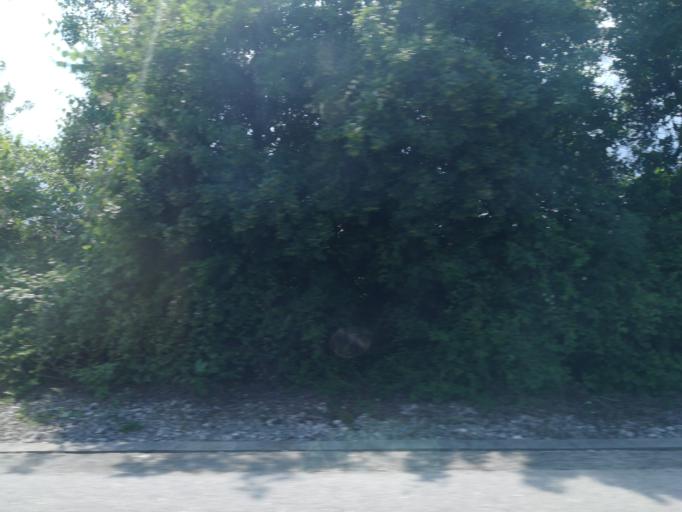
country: IT
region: Veneto
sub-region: Provincia di Vicenza
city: Novoledo
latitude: 45.6571
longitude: 11.5241
